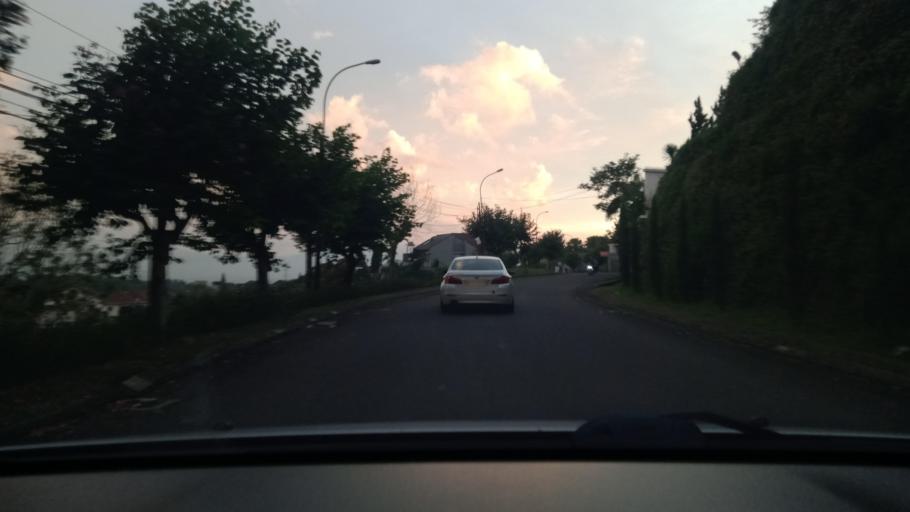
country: ID
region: West Java
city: Lembang
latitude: -6.8495
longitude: 107.5890
